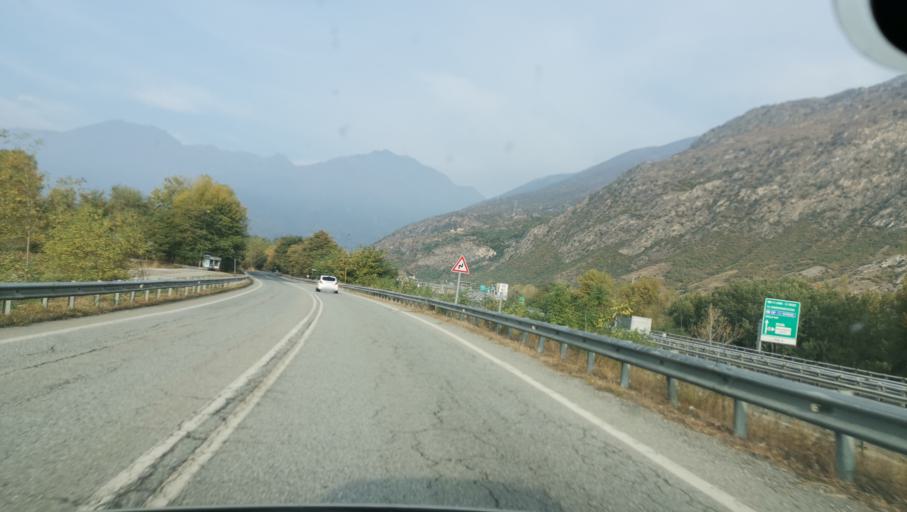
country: IT
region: Piedmont
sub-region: Provincia di Torino
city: Mattie
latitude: 45.1326
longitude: 7.1002
